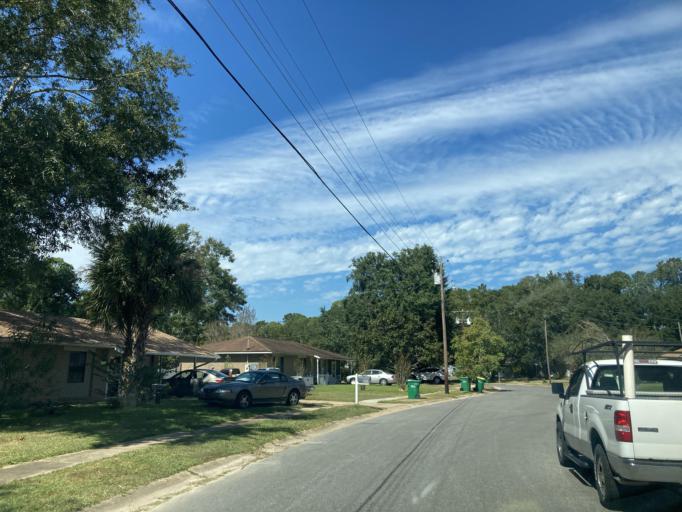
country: US
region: Mississippi
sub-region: Jackson County
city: Saint Martin
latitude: 30.4523
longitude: -88.8770
